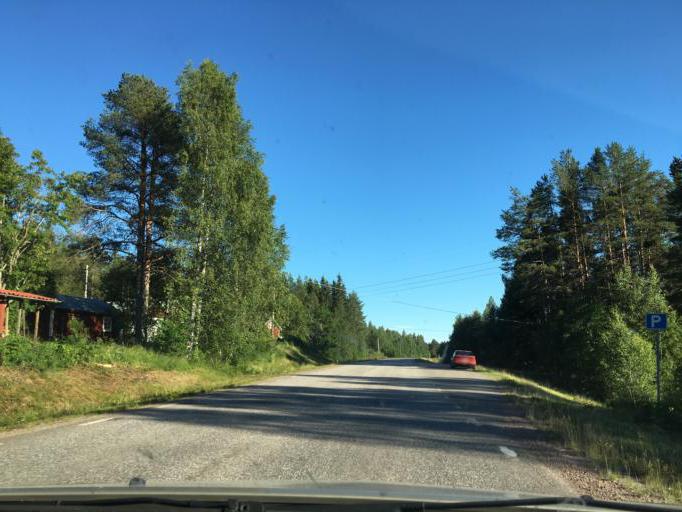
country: SE
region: Norrbotten
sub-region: Kalix Kommun
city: Rolfs
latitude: 65.9112
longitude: 22.9277
